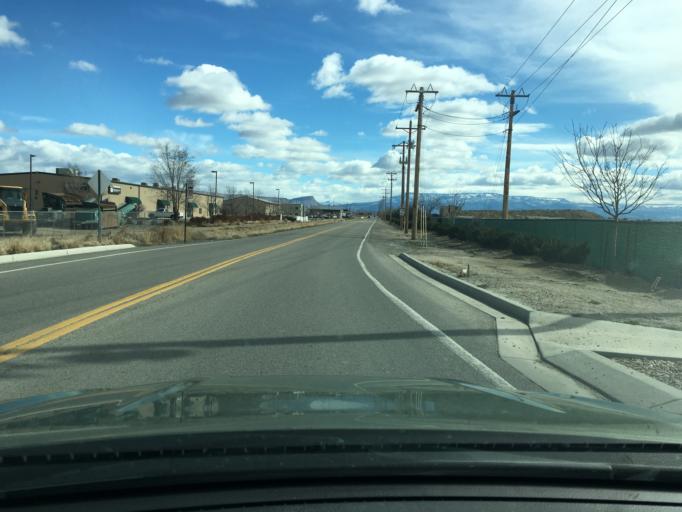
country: US
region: Colorado
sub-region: Mesa County
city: Redlands
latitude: 39.1062
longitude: -108.6263
